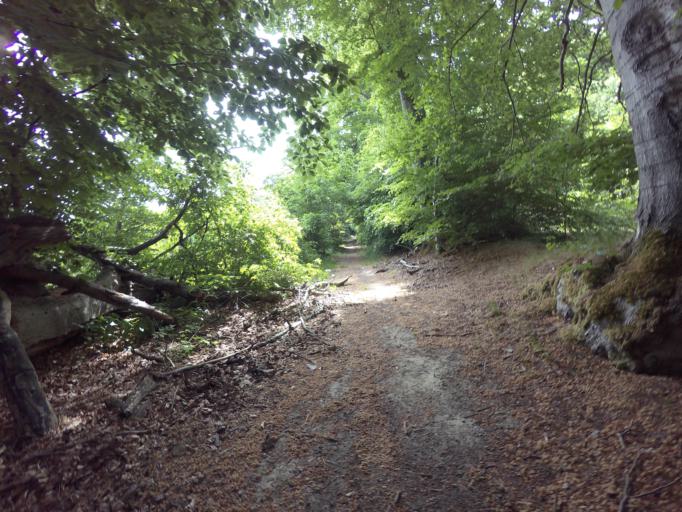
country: DE
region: Lower Saxony
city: Kneitlingen
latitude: 52.2040
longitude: 10.7503
